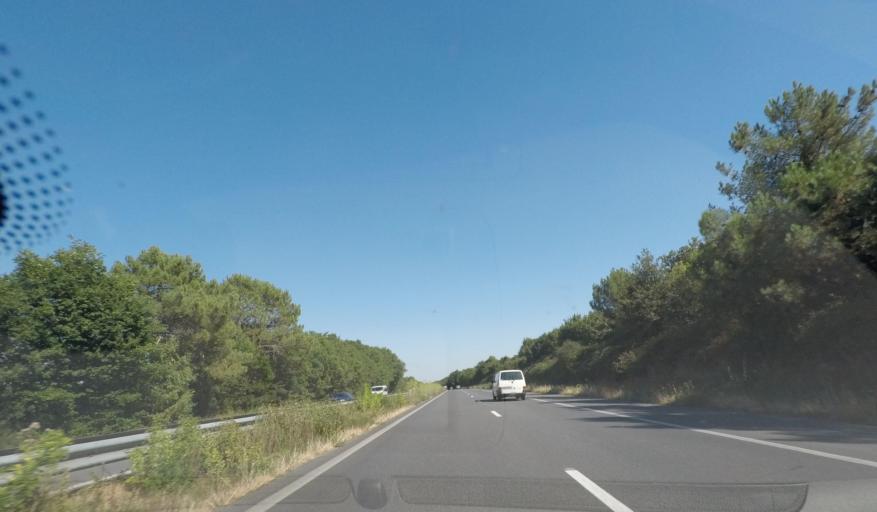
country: FR
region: Pays de la Loire
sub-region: Departement de la Loire-Atlantique
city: La Chapelle-des-Marais
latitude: 47.4892
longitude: -2.2307
